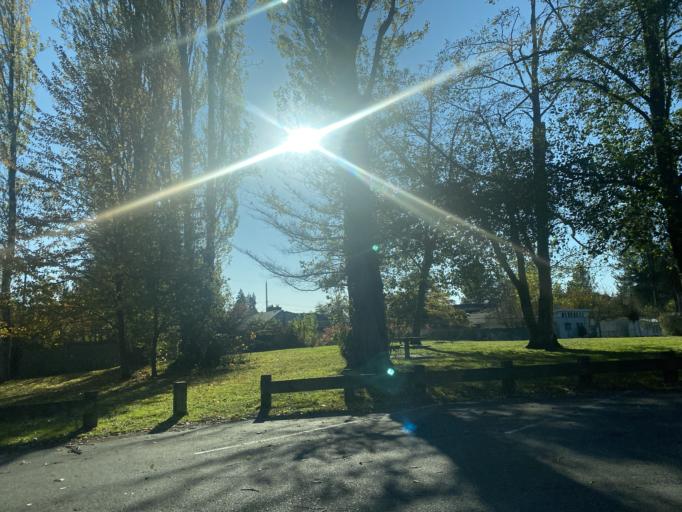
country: US
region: Washington
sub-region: Snohomish County
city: Esperance
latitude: 47.7673
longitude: -122.3629
